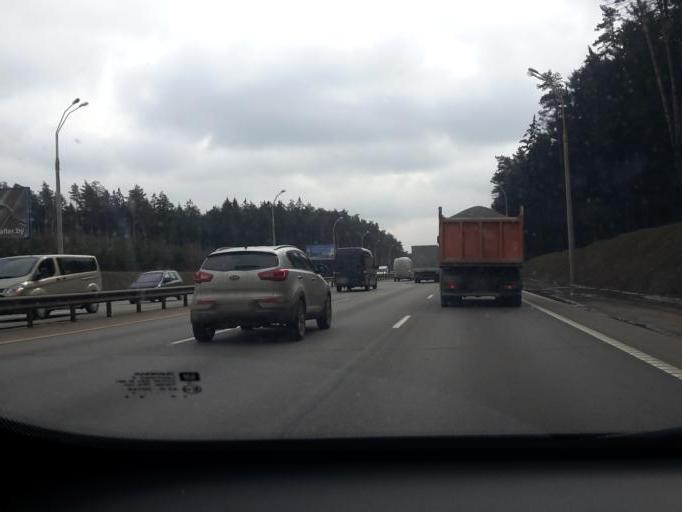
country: BY
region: Minsk
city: Borovlyany
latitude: 53.9505
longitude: 27.6529
